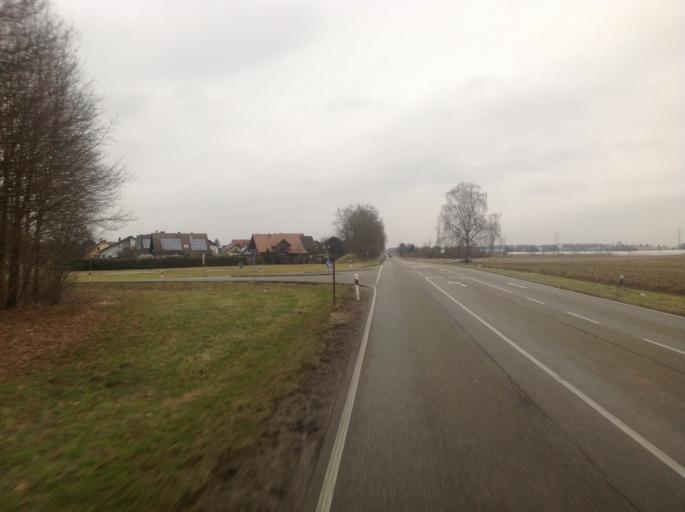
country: DE
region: Baden-Wuerttemberg
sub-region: Karlsruhe Region
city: Iffezheim
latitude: 48.8110
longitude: 8.1420
